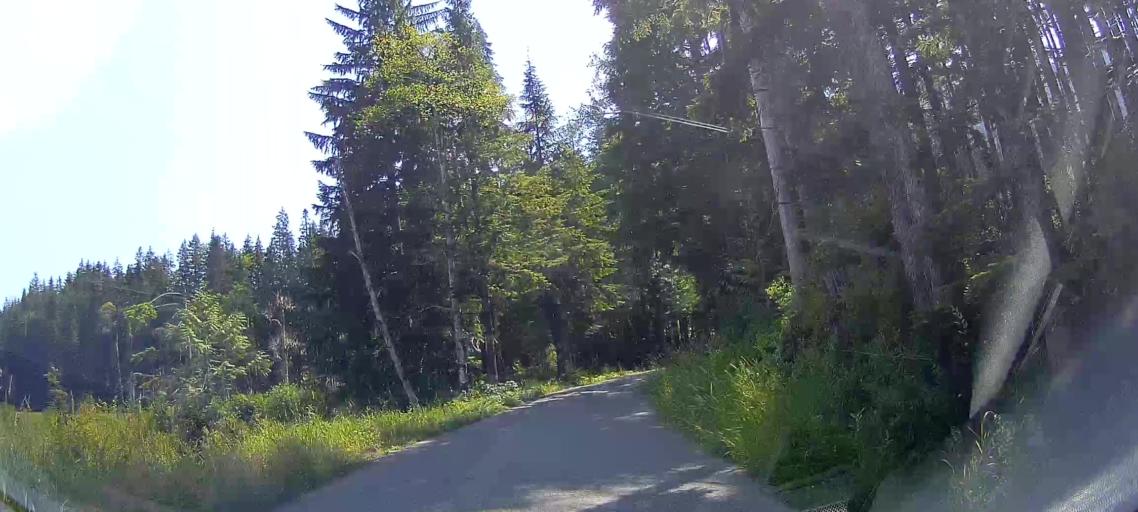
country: US
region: Washington
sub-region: Snohomish County
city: Arlington Heights
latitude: 48.3113
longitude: -121.9763
